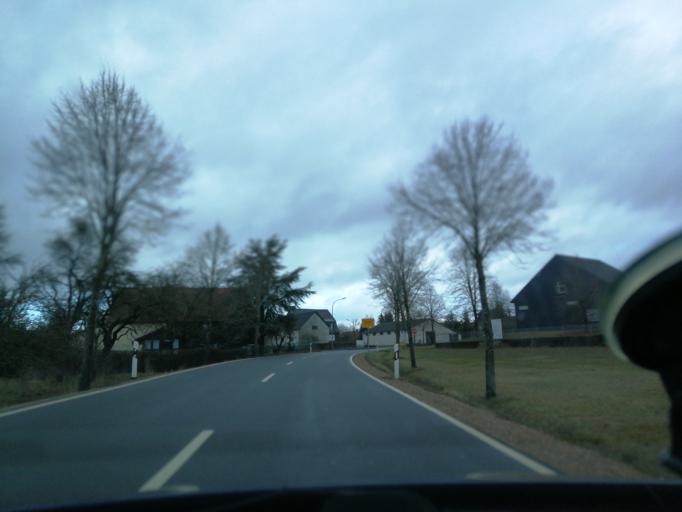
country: DE
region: Rheinland-Pfalz
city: Nohn
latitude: 50.3271
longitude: 6.7851
